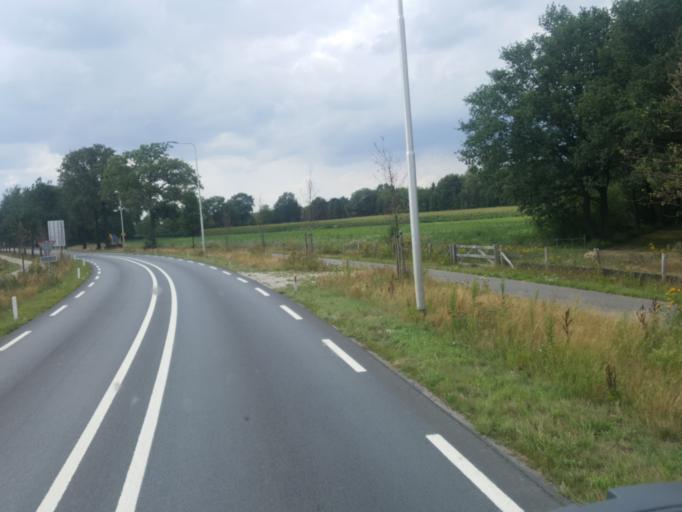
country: NL
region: North Brabant
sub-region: Gemeente Cuijk
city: Cuijk
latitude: 51.6829
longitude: 5.8414
